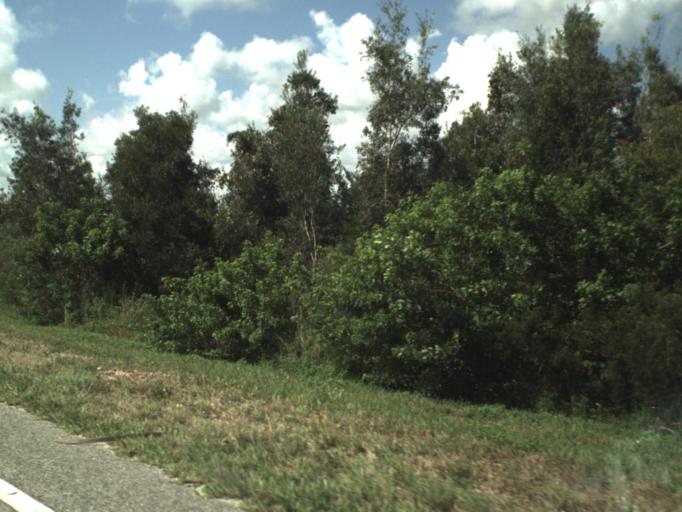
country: US
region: Florida
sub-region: Broward County
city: Weston
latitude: 26.0217
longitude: -80.4333
